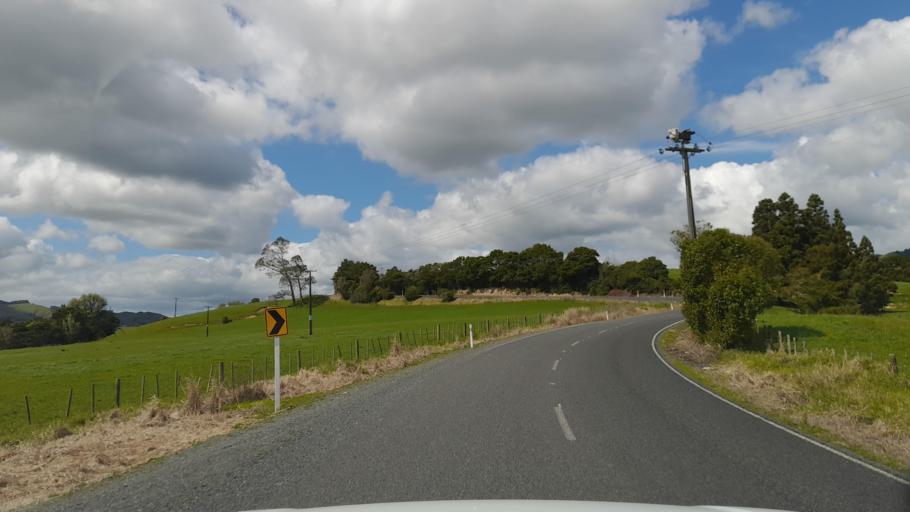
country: NZ
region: Northland
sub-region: Whangarei
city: Maungatapere
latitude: -35.6390
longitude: 174.0530
